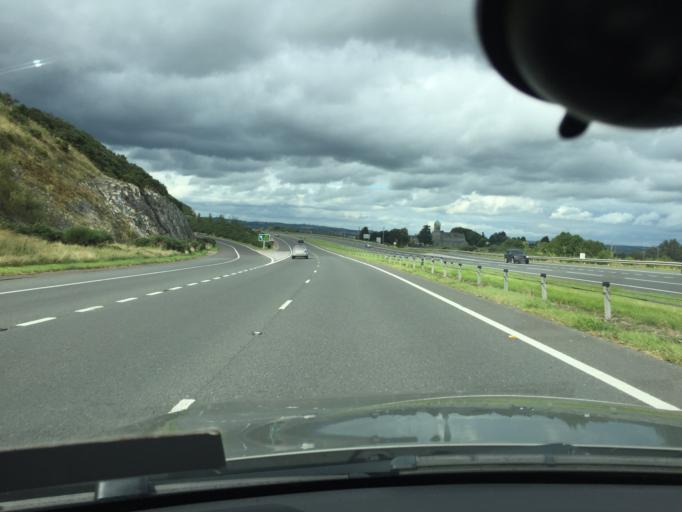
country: GB
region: Northern Ireland
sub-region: Newry and Mourne District
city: Newry
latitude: 54.1471
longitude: -6.3438
